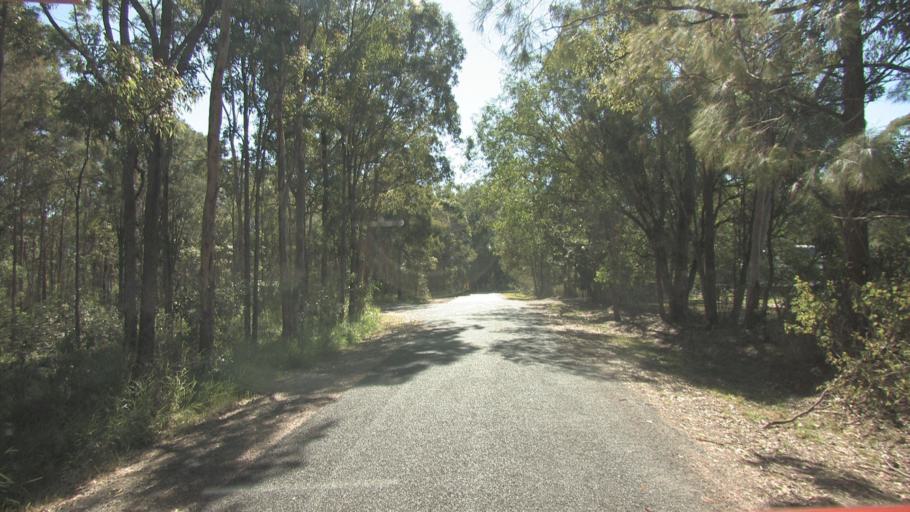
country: AU
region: Queensland
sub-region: Logan
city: Park Ridge South
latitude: -27.6881
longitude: 153.0060
